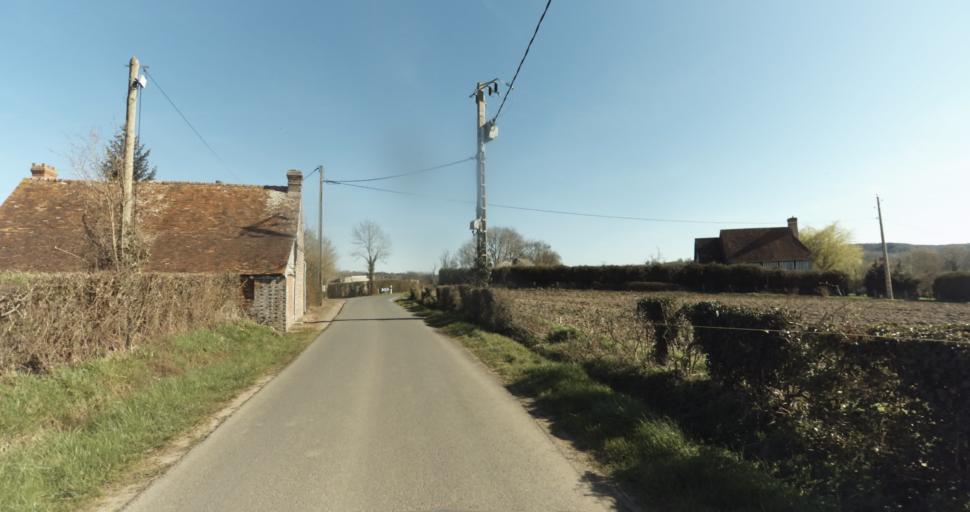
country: FR
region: Lower Normandy
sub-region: Departement du Calvados
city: Saint-Pierre-sur-Dives
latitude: 49.0311
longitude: 0.0572
